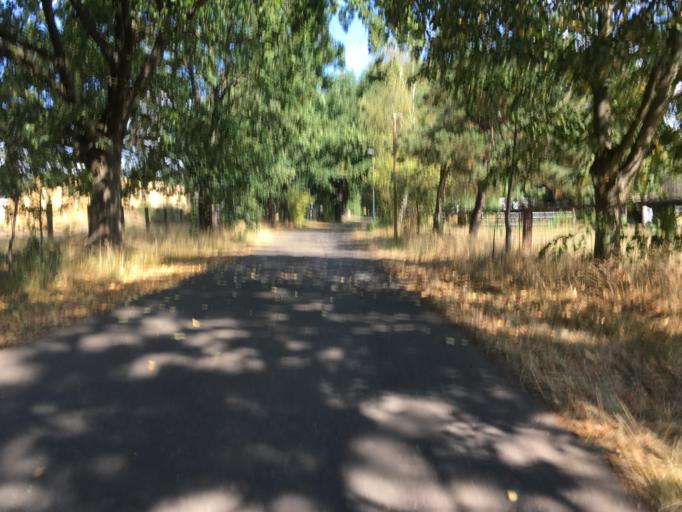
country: DE
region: Brandenburg
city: Zehdenick
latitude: 52.9879
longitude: 13.3787
